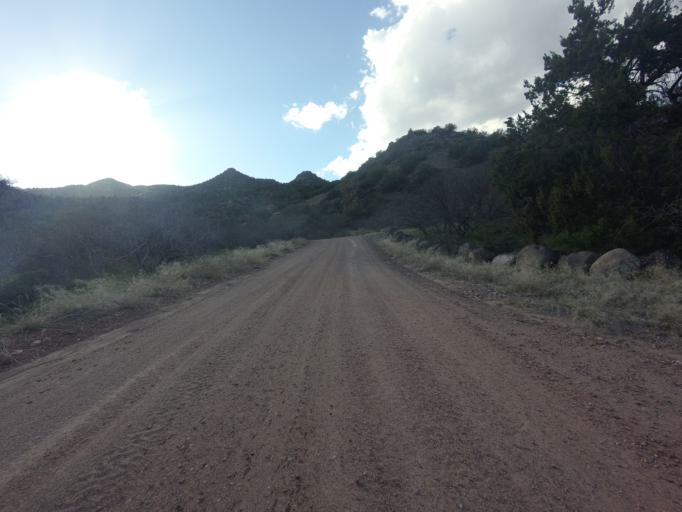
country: US
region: Arizona
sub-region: Gila County
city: Pine
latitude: 34.3878
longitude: -111.6569
